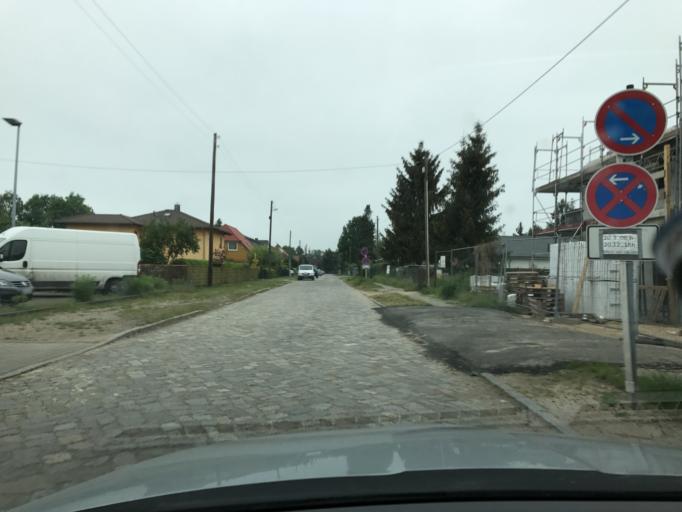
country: DE
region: Brandenburg
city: Falkensee
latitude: 52.5592
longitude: 13.0869
